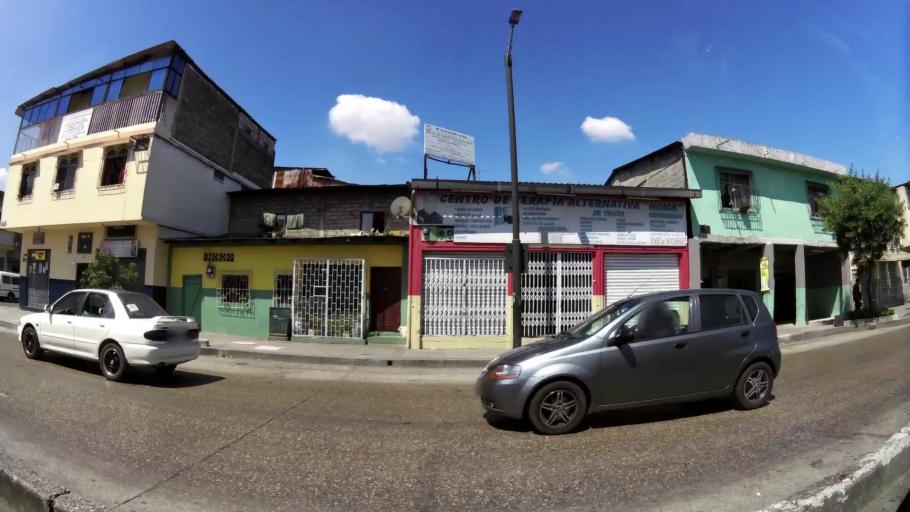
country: EC
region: Guayas
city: Guayaquil
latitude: -2.2084
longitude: -79.9280
